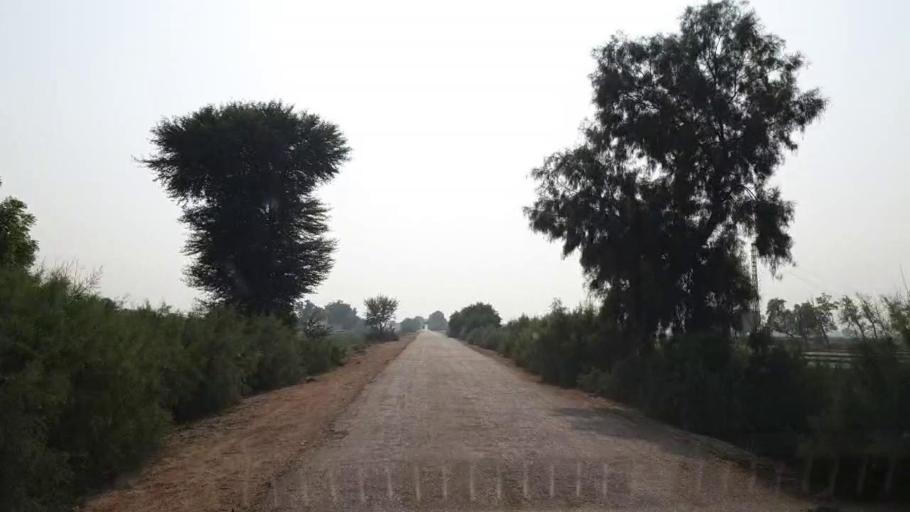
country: PK
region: Sindh
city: Bhan
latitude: 26.4804
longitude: 67.7704
